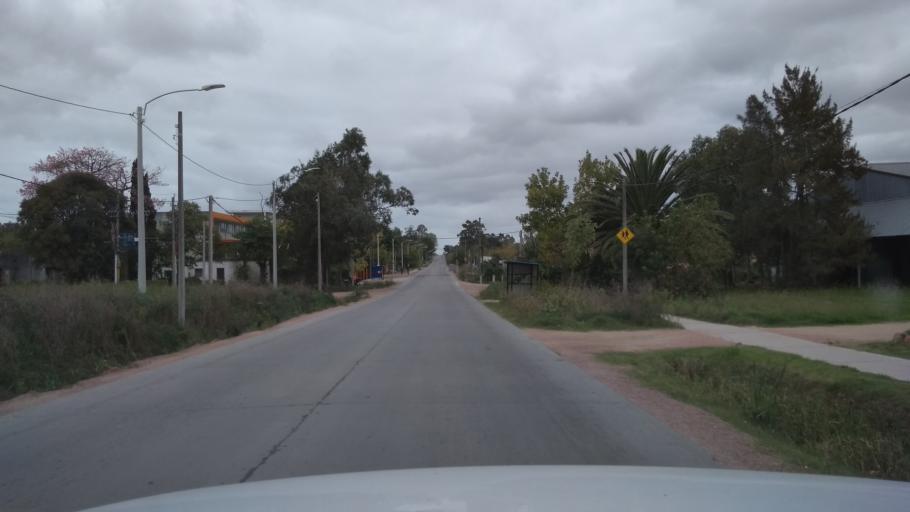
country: UY
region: Canelones
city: Toledo
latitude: -34.7829
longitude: -56.1382
